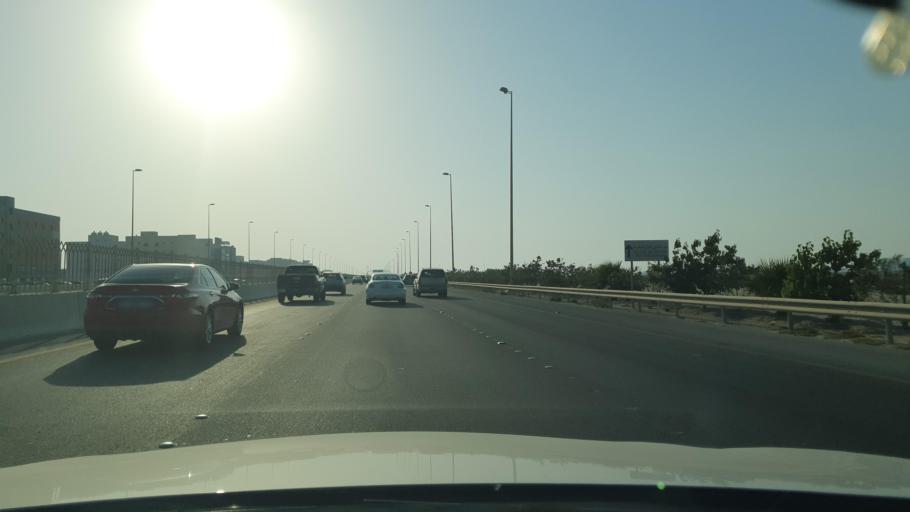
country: BH
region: Muharraq
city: Al Hadd
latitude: 26.2791
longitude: 50.6548
